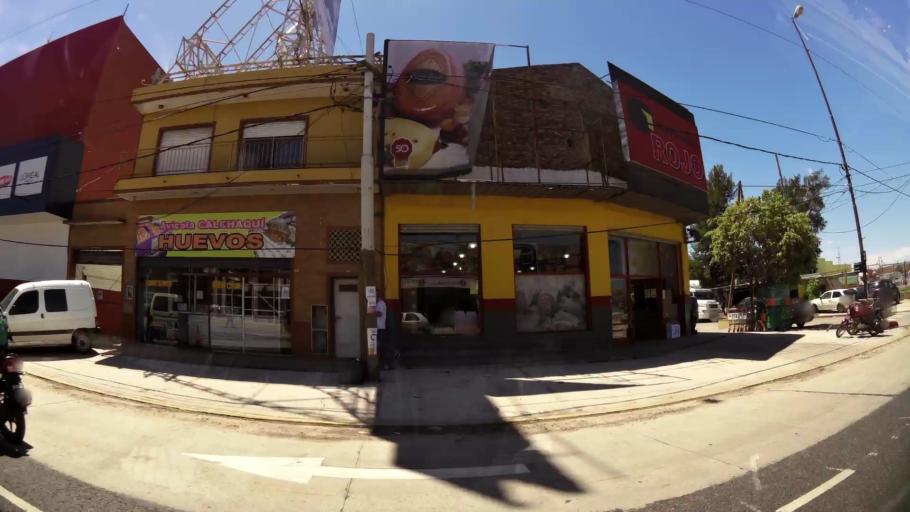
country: AR
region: Buenos Aires
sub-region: Partido de Quilmes
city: Quilmes
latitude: -34.7371
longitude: -58.2939
